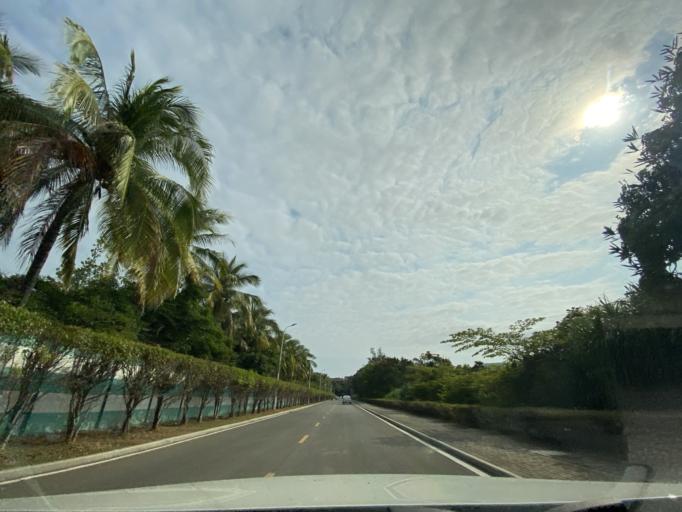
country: CN
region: Hainan
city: Tiandu
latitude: 18.2301
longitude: 109.6221
